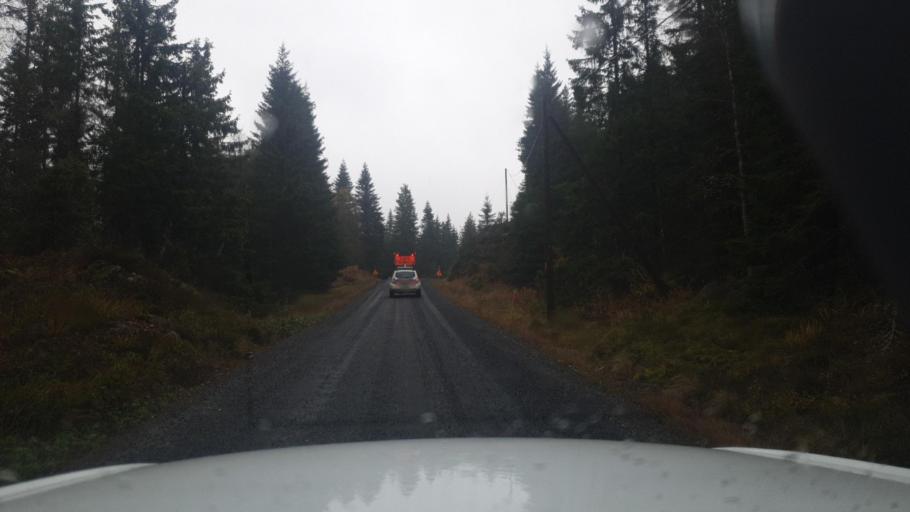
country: SE
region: Vaermland
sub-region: Torsby Kommun
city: Torsby
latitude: 60.1701
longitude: 12.6247
